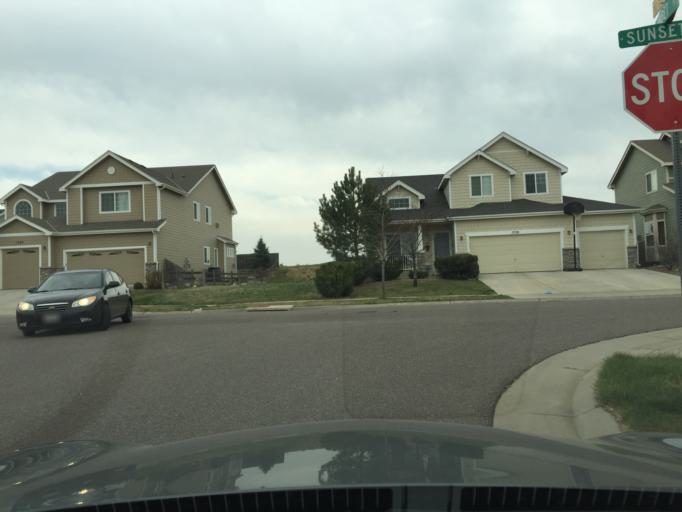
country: US
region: Colorado
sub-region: Boulder County
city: Erie
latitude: 40.0036
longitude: -105.0326
